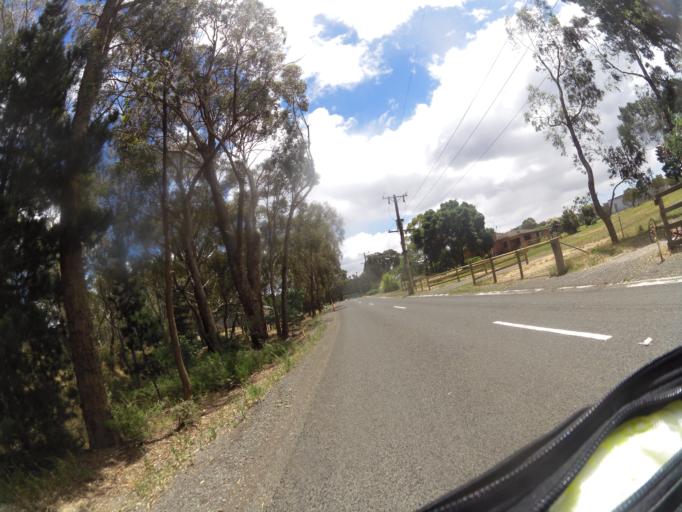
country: AU
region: Victoria
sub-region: Mount Alexander
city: Castlemaine
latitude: -37.0281
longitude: 144.2433
